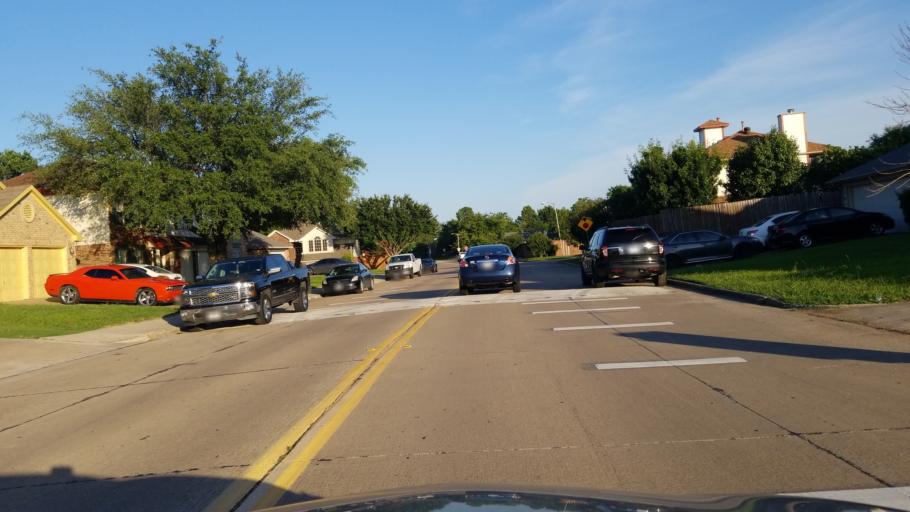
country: US
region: Texas
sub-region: Dallas County
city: Grand Prairie
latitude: 32.6907
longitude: -97.0114
